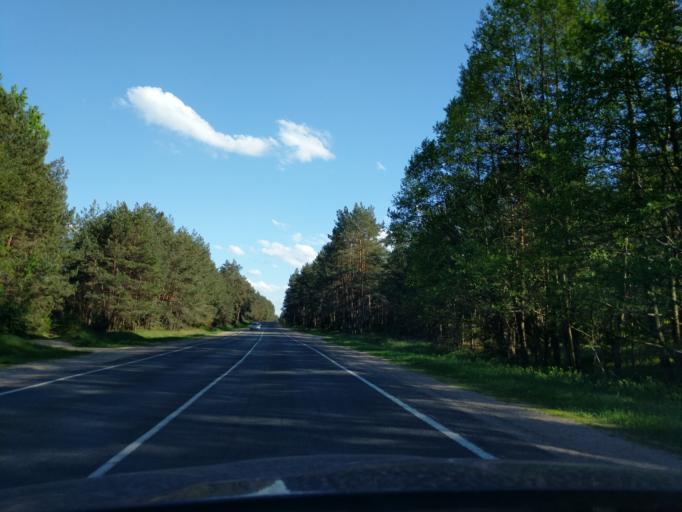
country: BY
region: Minsk
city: Myadzyel
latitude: 54.8425
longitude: 26.9269
